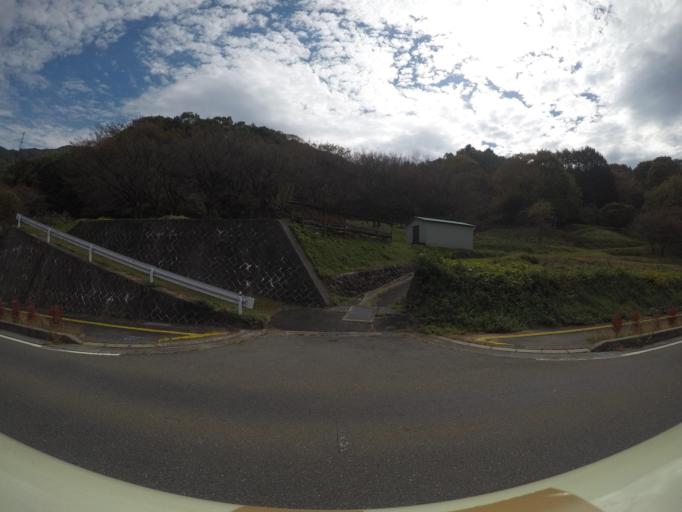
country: JP
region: Nagano
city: Ina
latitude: 35.8404
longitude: 138.0711
